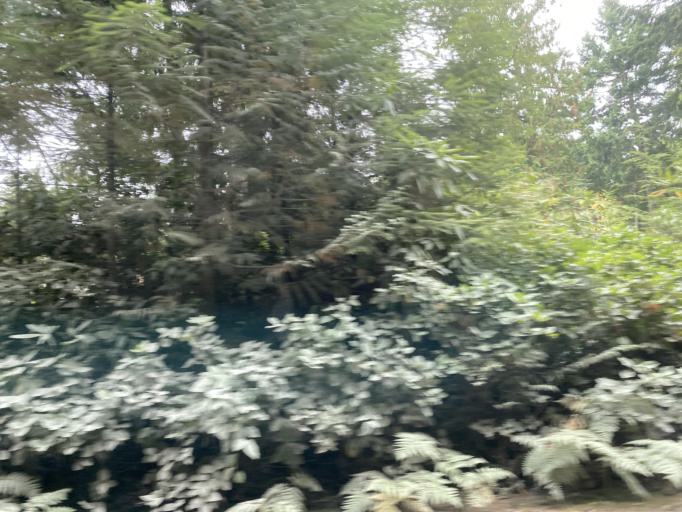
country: US
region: Washington
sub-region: Island County
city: Coupeville
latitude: 48.2117
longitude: -122.7300
